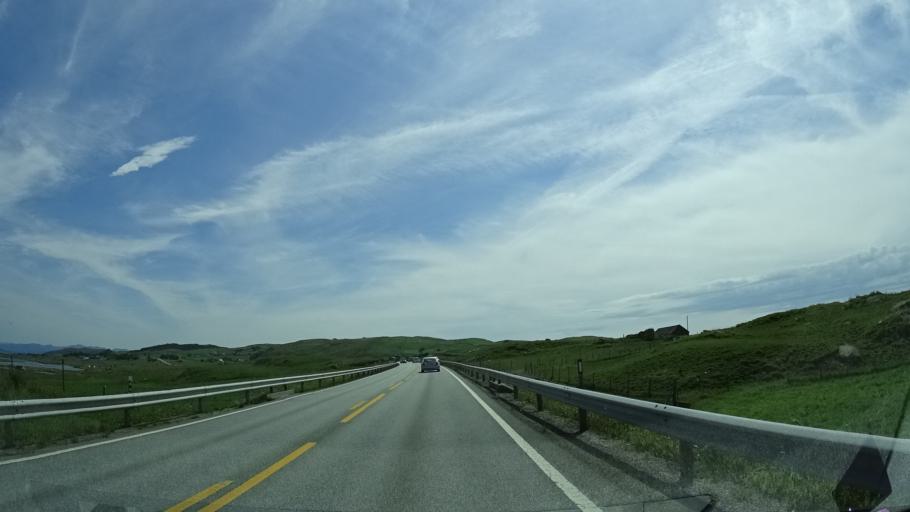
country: NO
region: Rogaland
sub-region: Rennesoy
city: Vikevag
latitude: 59.1321
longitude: 5.6086
